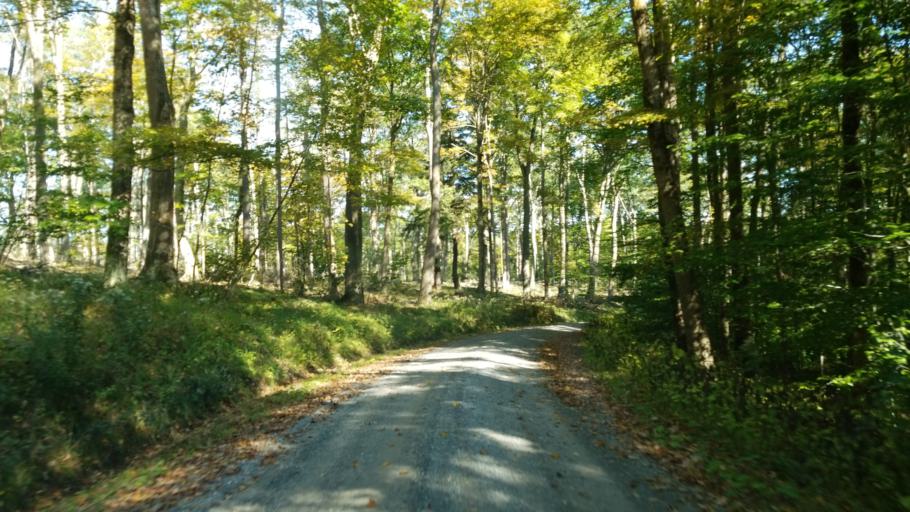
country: US
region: Pennsylvania
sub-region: Clearfield County
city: Treasure Lake
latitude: 41.1427
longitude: -78.5751
